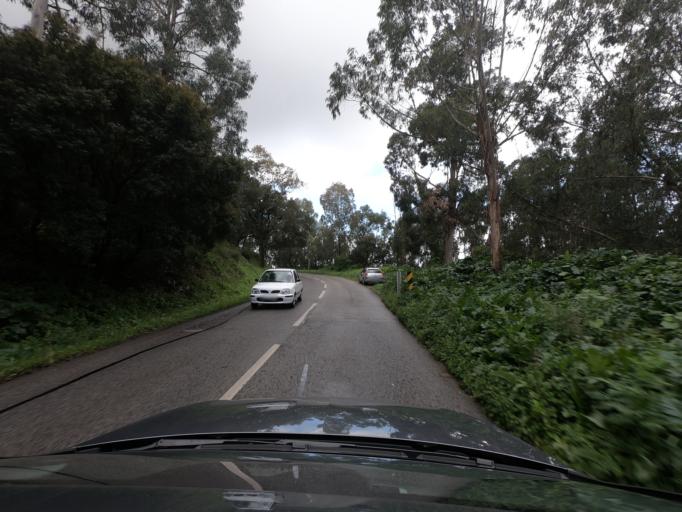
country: PT
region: Lisbon
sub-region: Sintra
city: Queluz
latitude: 38.7445
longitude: -9.2626
